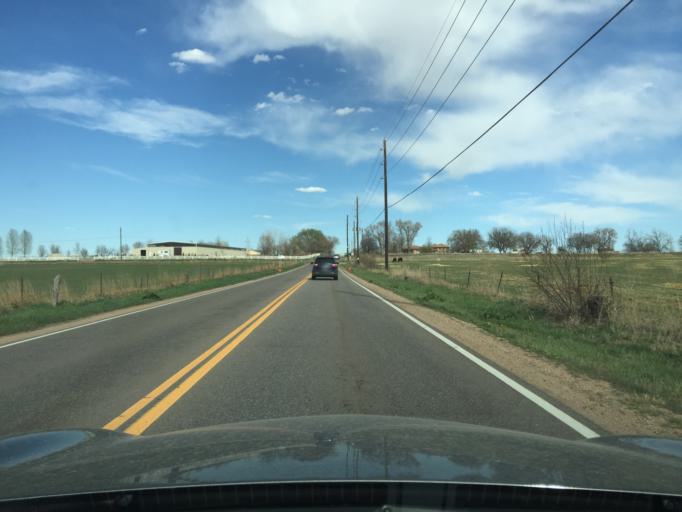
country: US
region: Colorado
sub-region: Boulder County
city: Lafayette
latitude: 40.0366
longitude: -105.1004
